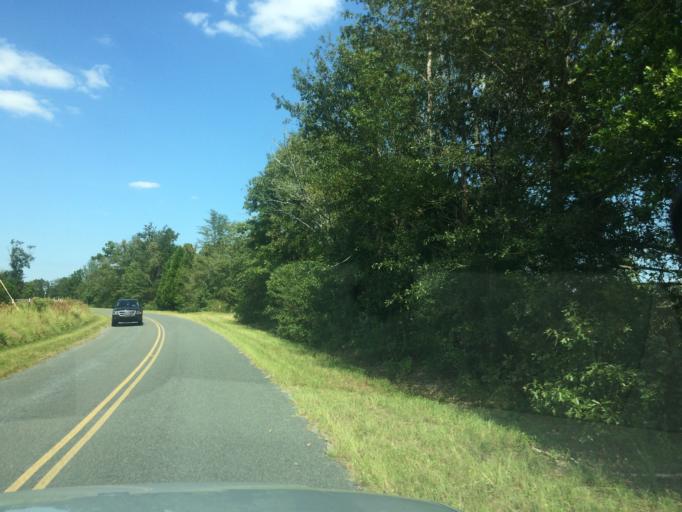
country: US
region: South Carolina
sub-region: Barnwell County
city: Williston
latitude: 33.6117
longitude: -81.4769
